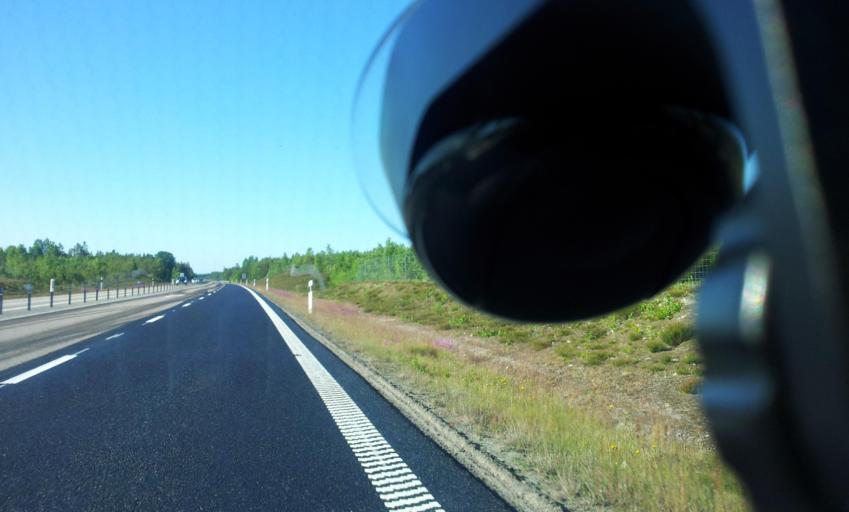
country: SE
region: Kalmar
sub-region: Torsas Kommun
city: Torsas
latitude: 56.4834
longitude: 16.0823
